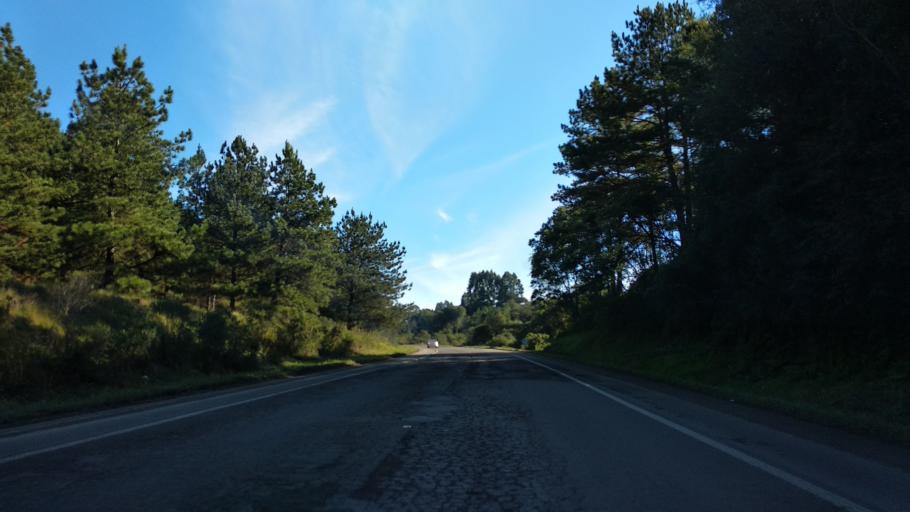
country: BR
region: Santa Catarina
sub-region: Campos Novos
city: Campos Novos
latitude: -27.4001
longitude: -51.1993
